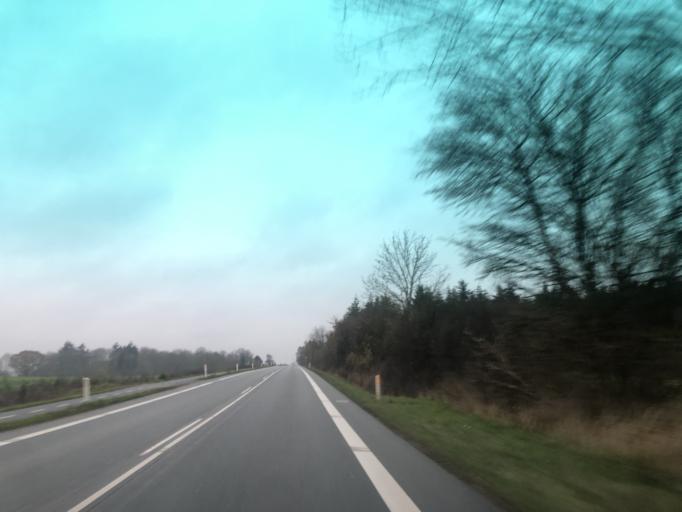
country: DK
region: South Denmark
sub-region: Nyborg Kommune
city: Nyborg
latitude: 55.2979
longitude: 10.7153
